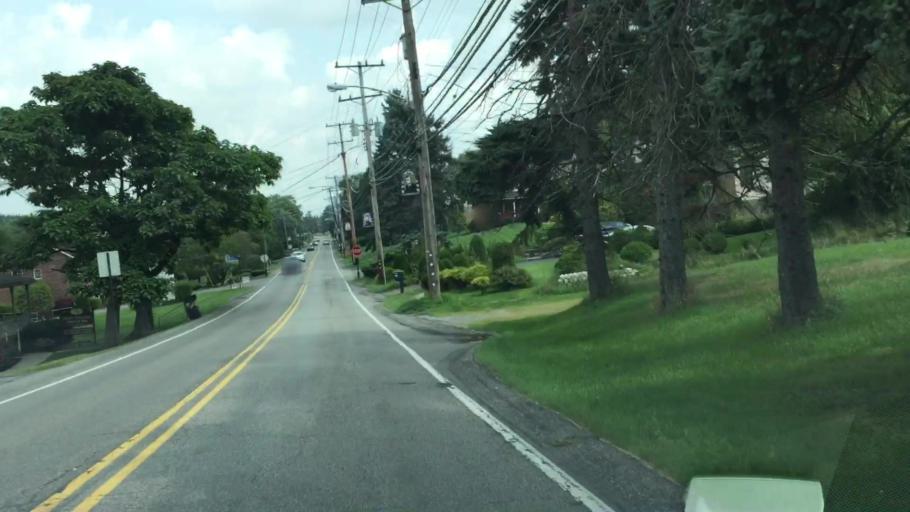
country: US
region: Pennsylvania
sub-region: Allegheny County
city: Coraopolis
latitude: 40.4694
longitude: -80.1367
